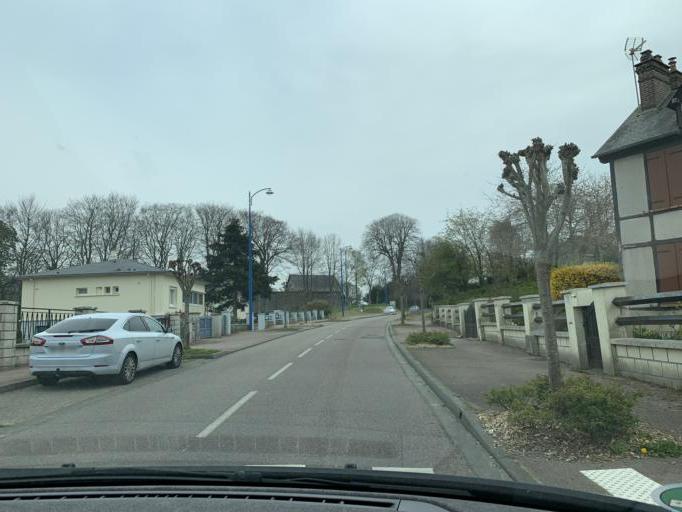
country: FR
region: Haute-Normandie
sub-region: Departement de la Seine-Maritime
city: Saint-Valery-en-Caux
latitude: 49.8594
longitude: 0.7196
